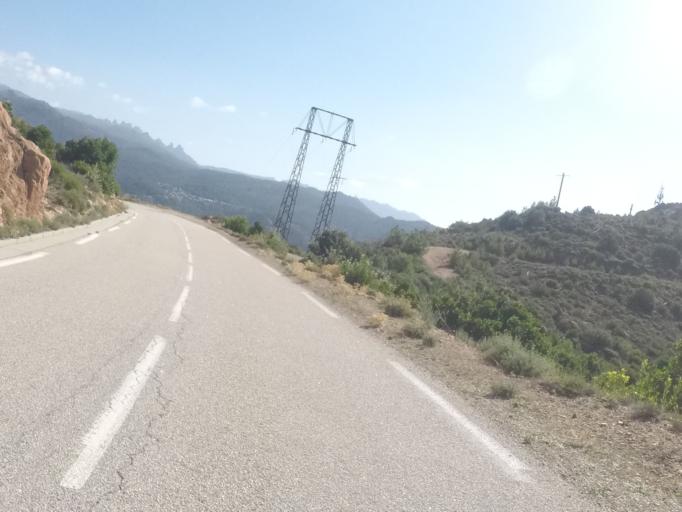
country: FR
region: Corsica
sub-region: Departement de la Corse-du-Sud
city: Olmeto
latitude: 41.7645
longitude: 9.0403
